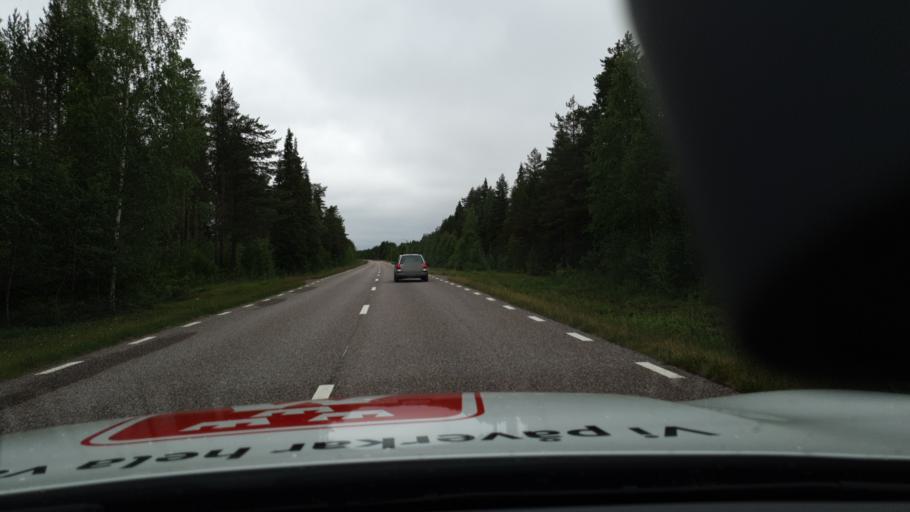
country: FI
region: Lapland
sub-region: Torniolaakso
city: Pello
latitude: 67.0016
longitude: 23.7564
